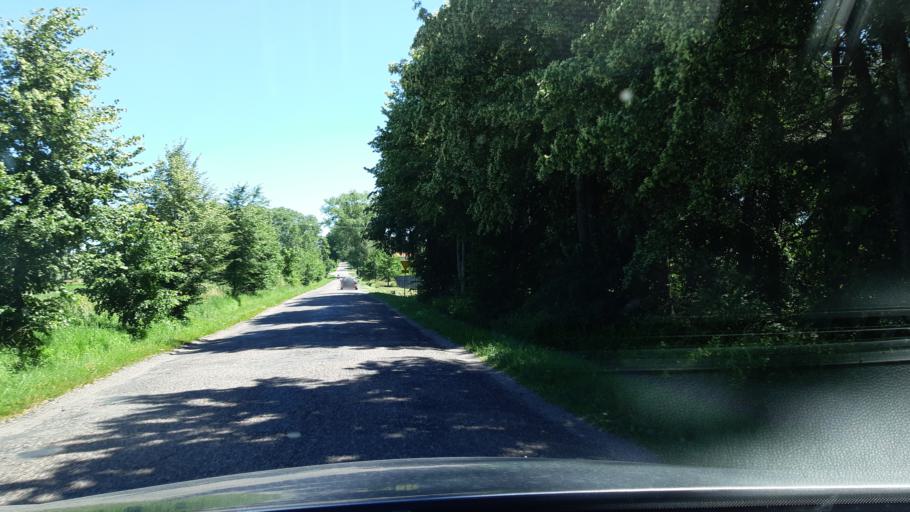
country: PL
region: Warmian-Masurian Voivodeship
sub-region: Powiat gizycki
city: Gizycko
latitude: 53.9495
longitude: 21.7606
